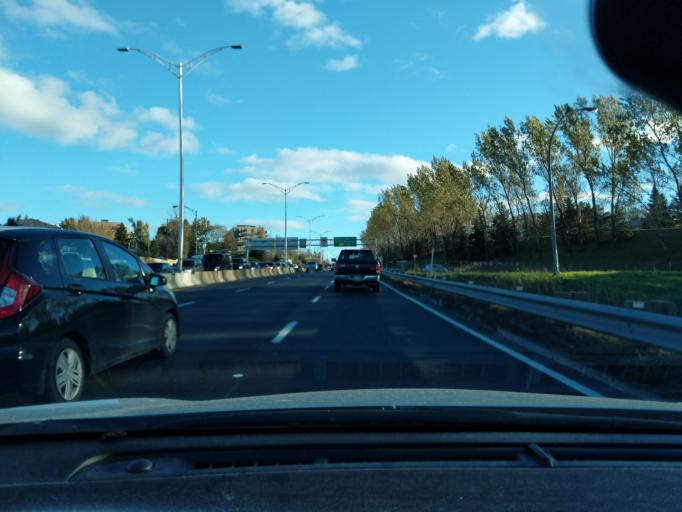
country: CA
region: Quebec
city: L'Ancienne-Lorette
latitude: 46.7812
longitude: -71.3091
